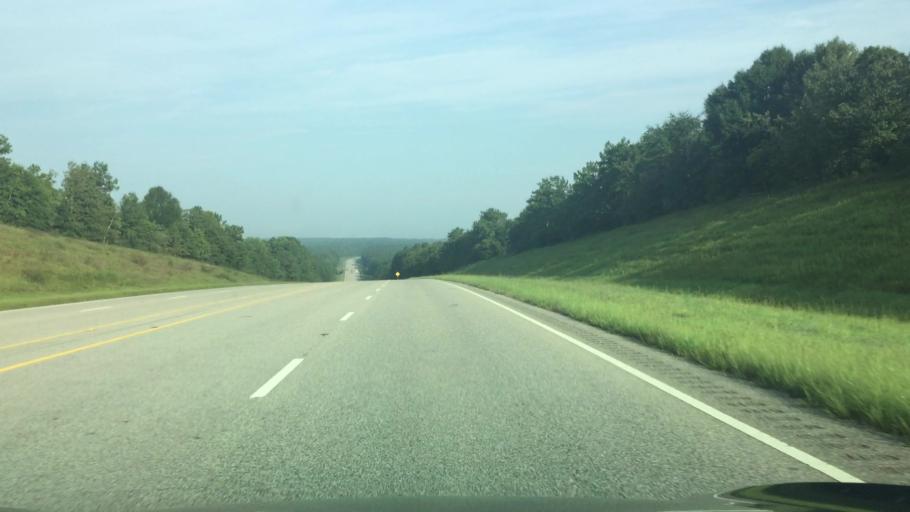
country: US
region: Alabama
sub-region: Butler County
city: Georgiana
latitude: 31.4617
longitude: -86.6452
